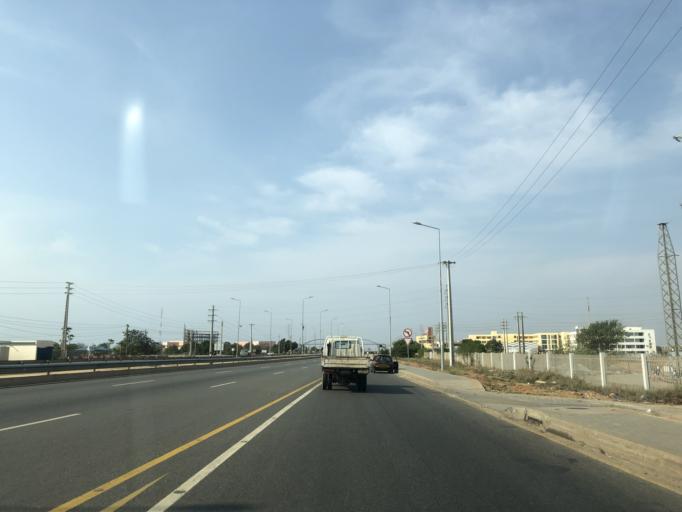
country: AO
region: Luanda
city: Luanda
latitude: -8.9705
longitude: 13.2549
